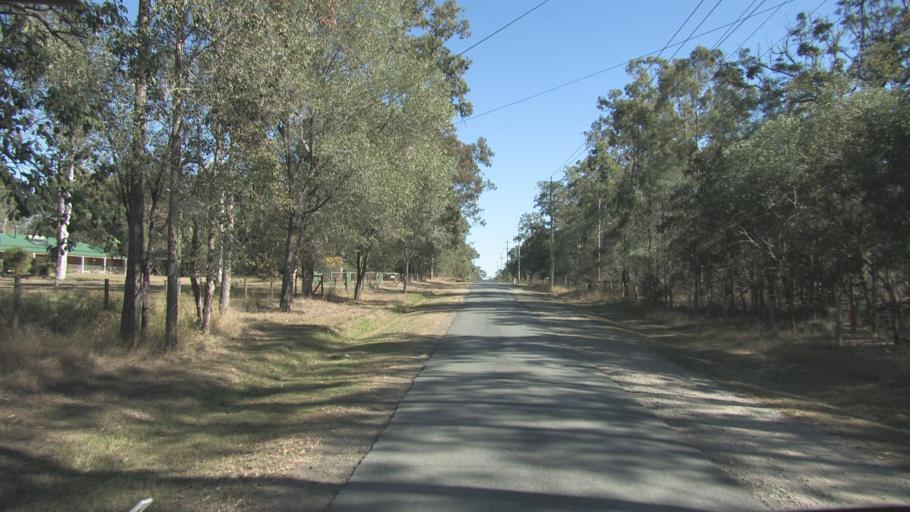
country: AU
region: Queensland
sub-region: Logan
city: North Maclean
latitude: -27.7999
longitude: 153.0546
